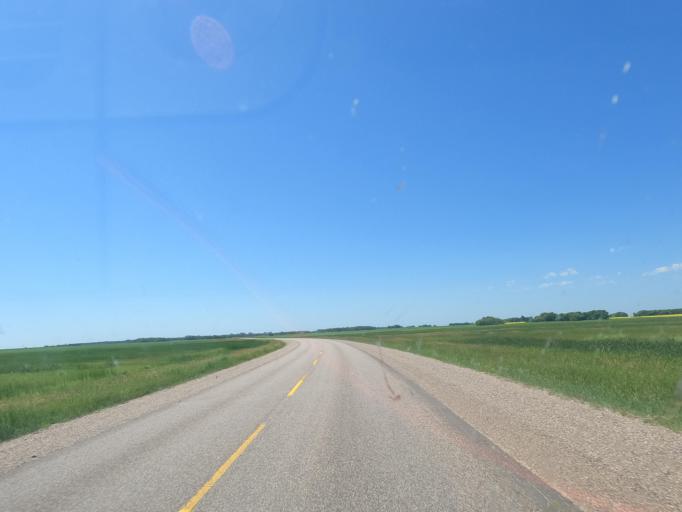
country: CA
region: Manitoba
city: Souris
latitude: 49.6203
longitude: -100.5194
